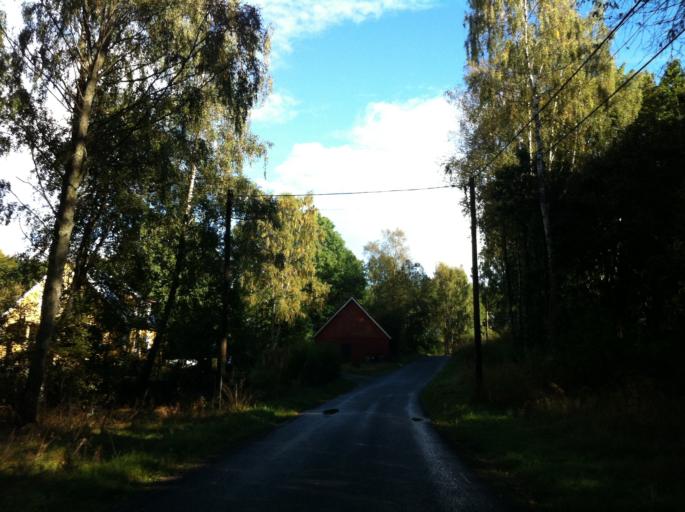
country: SE
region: Skane
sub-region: Perstorps Kommun
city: Perstorp
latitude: 56.1405
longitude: 13.5253
